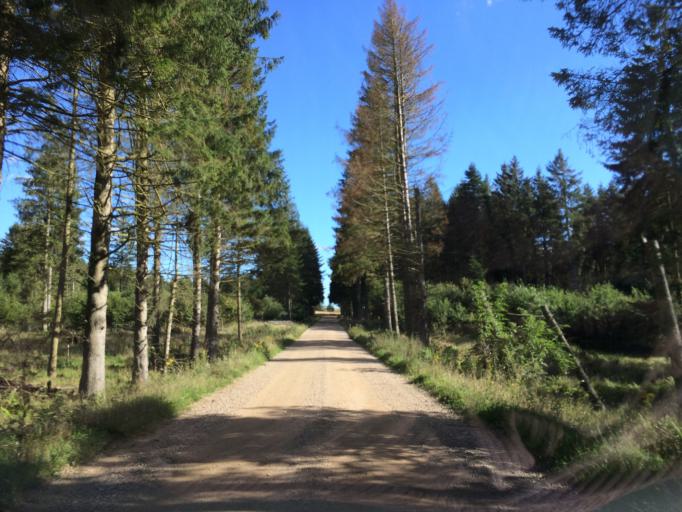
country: DK
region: Central Jutland
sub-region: Holstebro Kommune
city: Ulfborg
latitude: 56.2791
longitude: 8.4758
